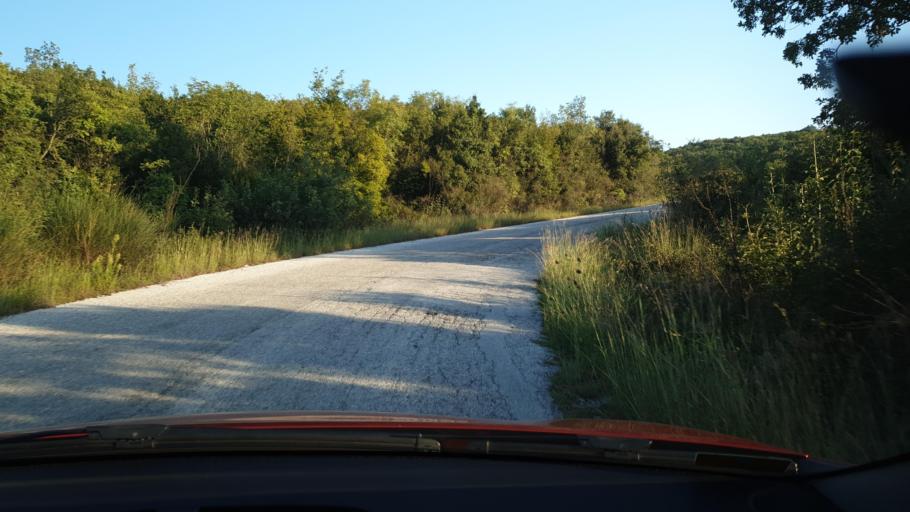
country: GR
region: Central Macedonia
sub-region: Nomos Chalkidikis
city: Galatista
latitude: 40.5558
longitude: 23.2848
